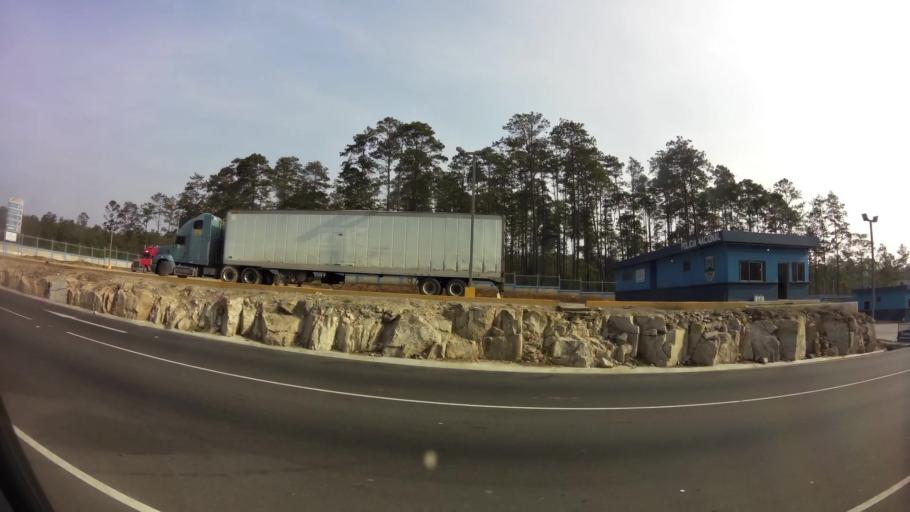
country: HN
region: Francisco Morazan
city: Zambrano
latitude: 14.2914
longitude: -87.4342
